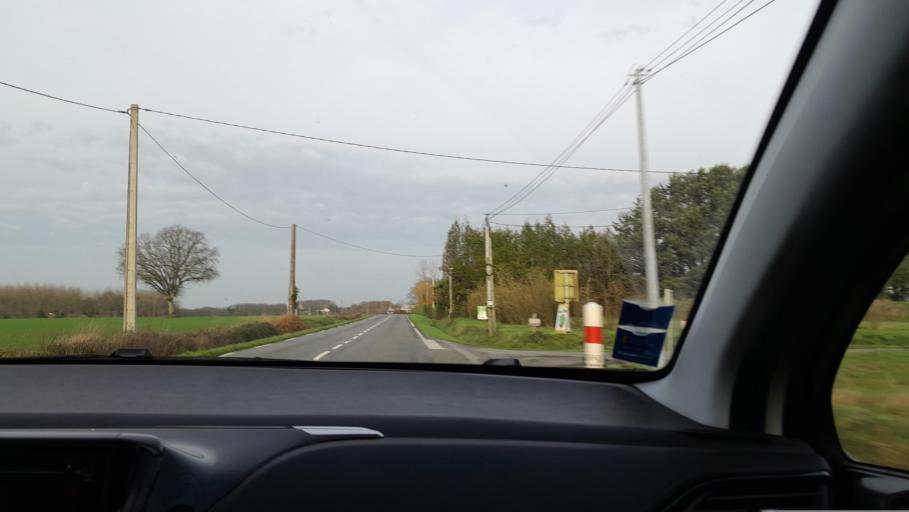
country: FR
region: Brittany
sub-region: Departement d'Ille-et-Vilaine
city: La Guerche-de-Bretagne
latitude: 47.9115
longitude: -1.1984
